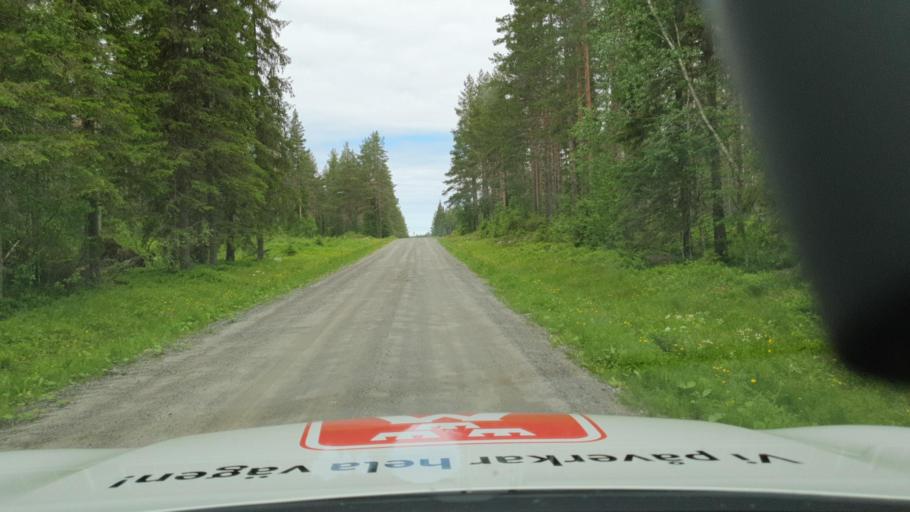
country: SE
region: Vaesterbotten
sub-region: Skelleftea Kommun
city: Langsele
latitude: 64.4631
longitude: 20.2767
